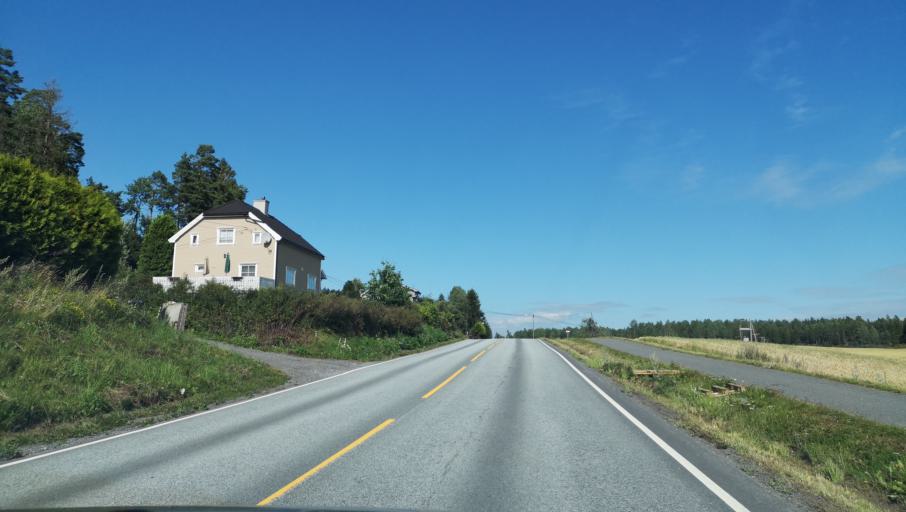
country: NO
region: Ostfold
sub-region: Valer
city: Kirkebygda
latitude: 59.5609
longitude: 10.8497
